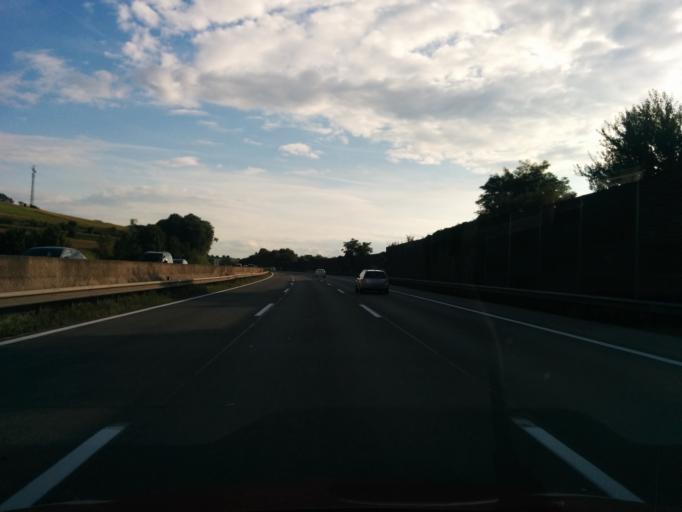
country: AT
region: Lower Austria
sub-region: Politischer Bezirk Melk
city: Erlauf
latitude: 48.1848
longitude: 15.1902
